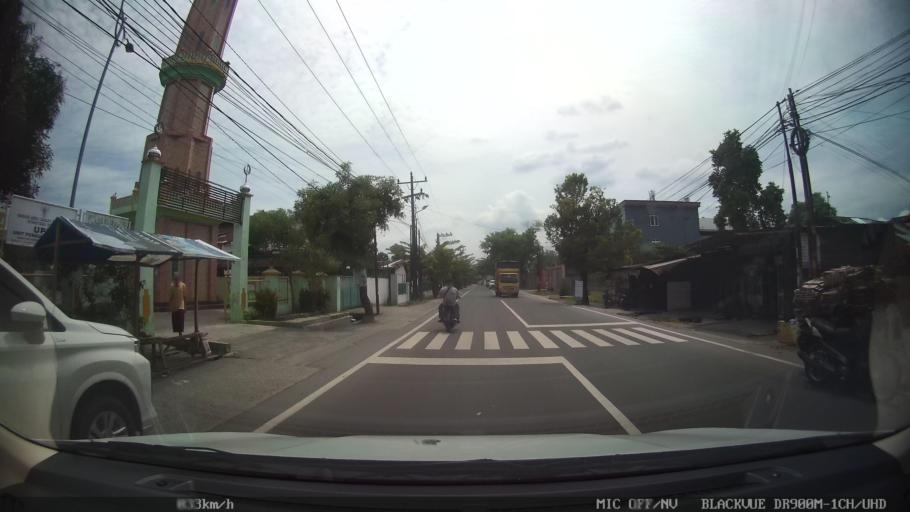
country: ID
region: North Sumatra
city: Sunggal
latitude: 3.5778
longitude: 98.6244
